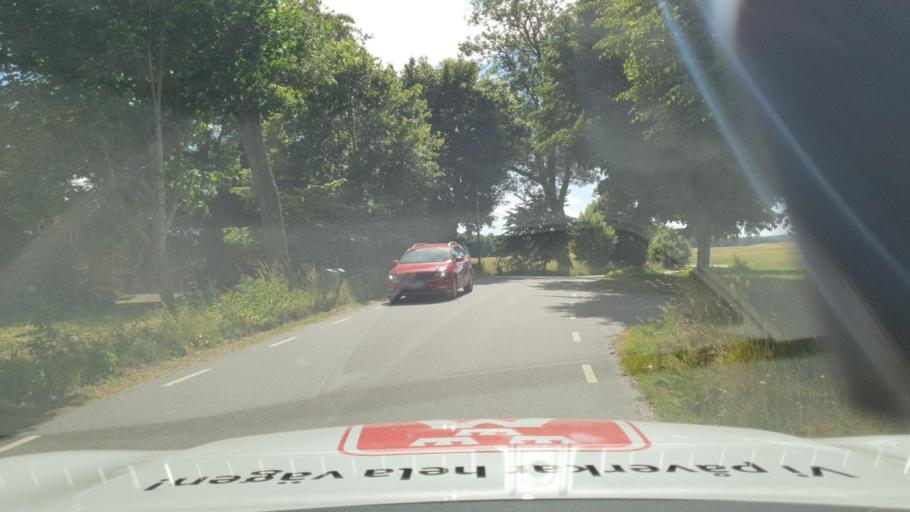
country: SE
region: Skane
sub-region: Sjobo Kommun
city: Blentarp
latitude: 55.6073
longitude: 13.5874
